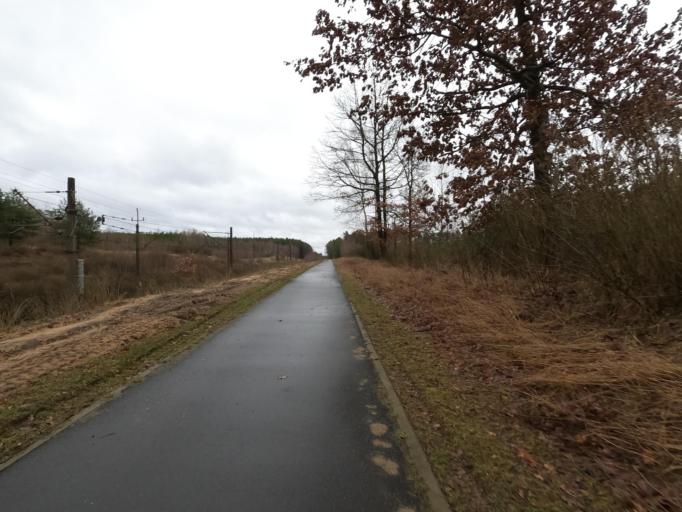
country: PL
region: Greater Poland Voivodeship
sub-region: Powiat pilski
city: Kaczory
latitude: 53.1221
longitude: 16.8212
